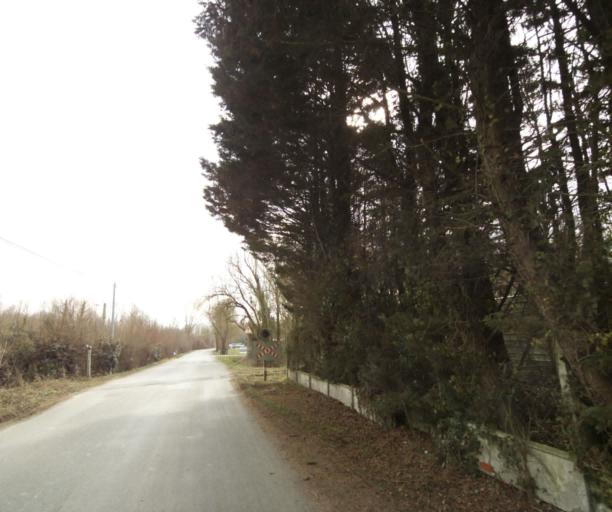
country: FR
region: Poitou-Charentes
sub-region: Departement des Deux-Sevres
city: Niort
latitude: 46.3043
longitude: -0.4538
